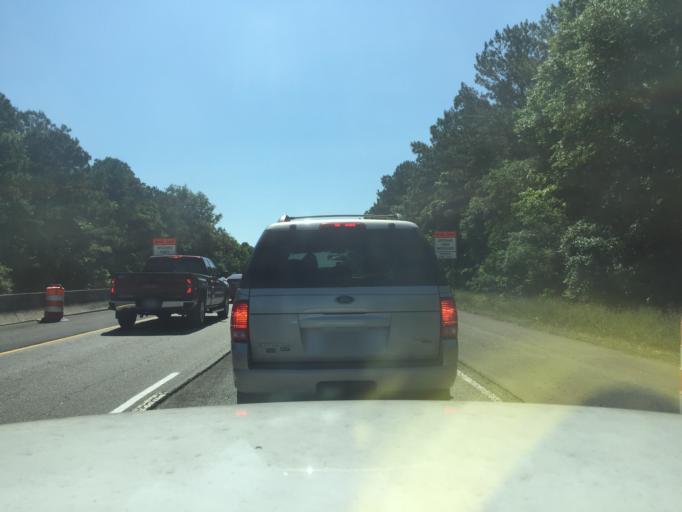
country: US
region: Georgia
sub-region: Chatham County
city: Georgetown
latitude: 31.9943
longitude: -81.2346
